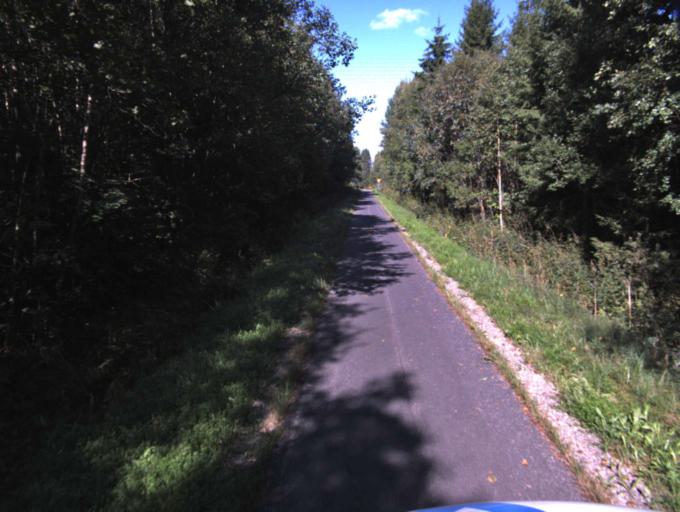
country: SE
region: Vaestra Goetaland
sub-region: Ulricehamns Kommun
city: Ulricehamn
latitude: 57.8112
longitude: 13.3549
